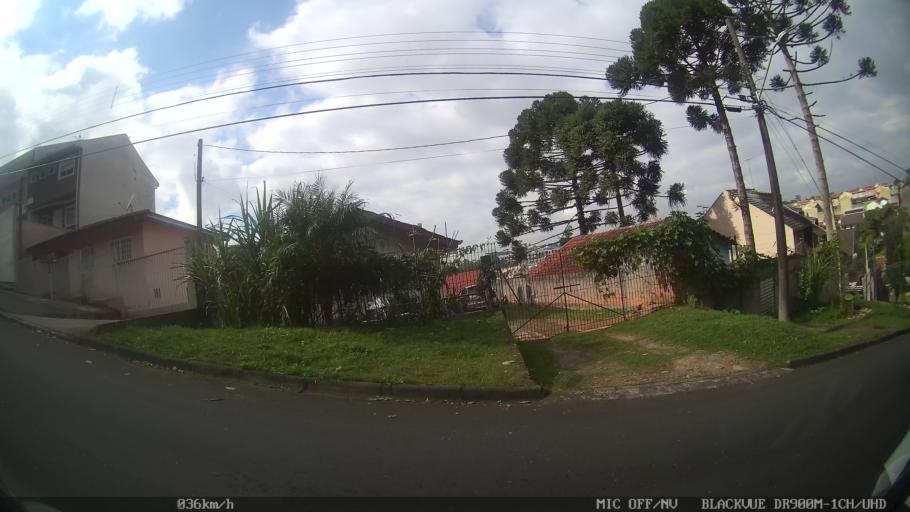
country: BR
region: Parana
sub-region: Curitiba
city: Curitiba
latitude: -25.3716
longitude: -49.2559
